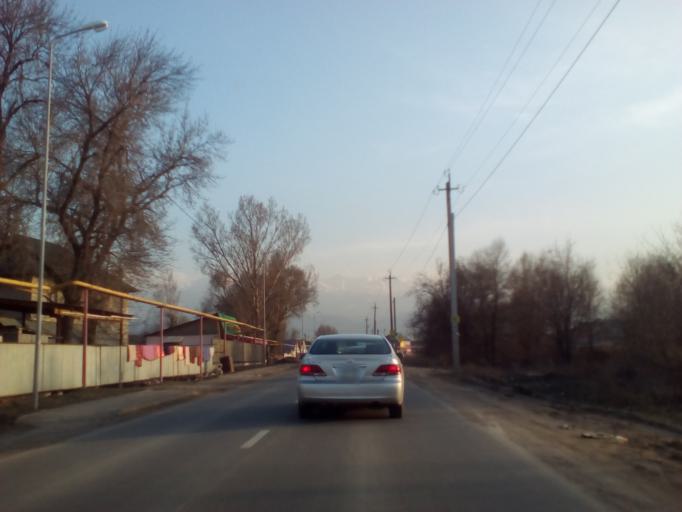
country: KZ
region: Almaty Oblysy
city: Burunday
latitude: 43.2433
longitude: 76.7463
